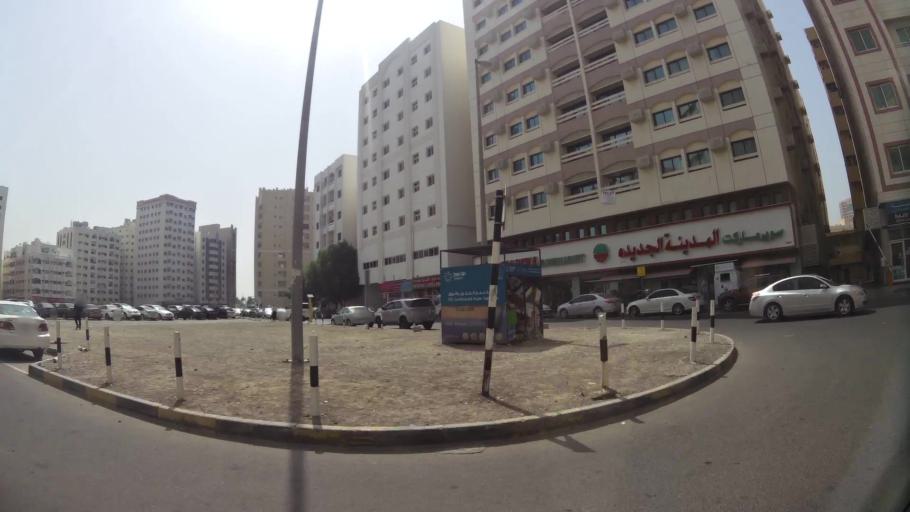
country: AE
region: Ash Shariqah
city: Sharjah
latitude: 25.3513
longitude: 55.3896
